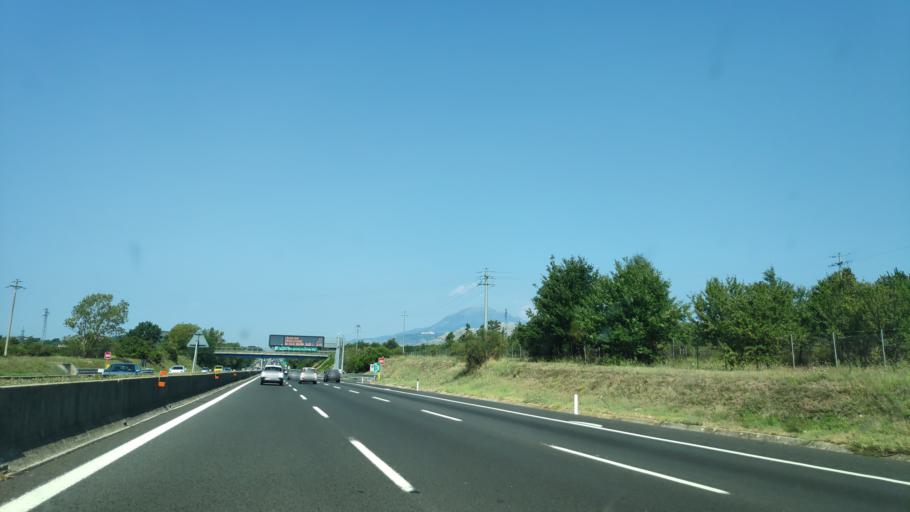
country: IT
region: Campania
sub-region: Provincia di Caserta
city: Bivio Mortola
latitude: 41.4256
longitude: 13.9165
